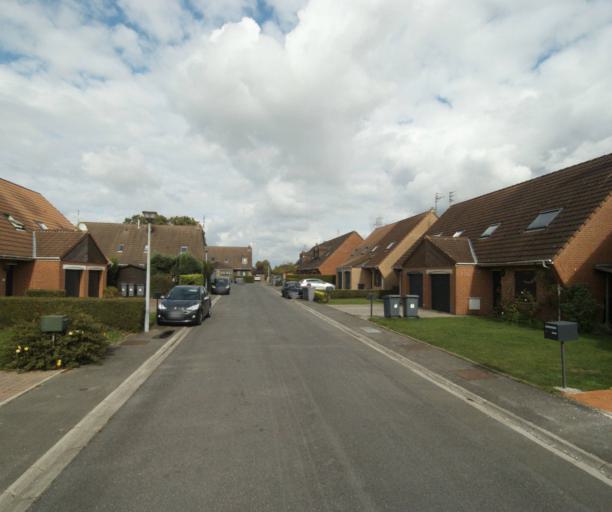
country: FR
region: Nord-Pas-de-Calais
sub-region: Departement du Nord
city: Premesques
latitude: 50.6541
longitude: 2.9546
